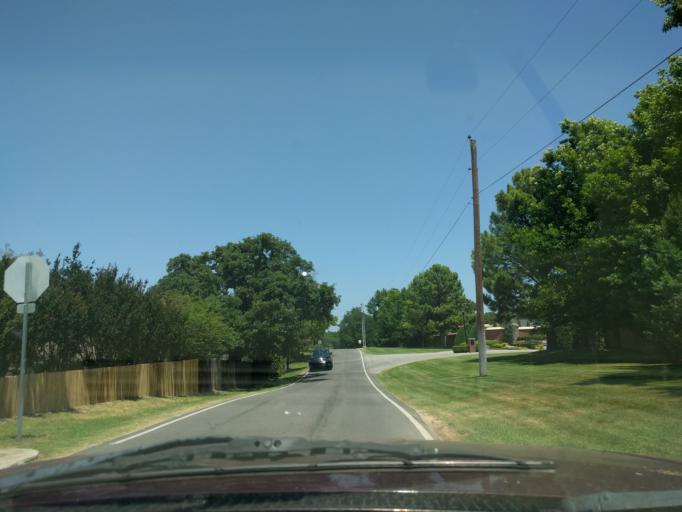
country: US
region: Oklahoma
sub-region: Tulsa County
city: Jenks
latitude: 36.0051
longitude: -95.9356
